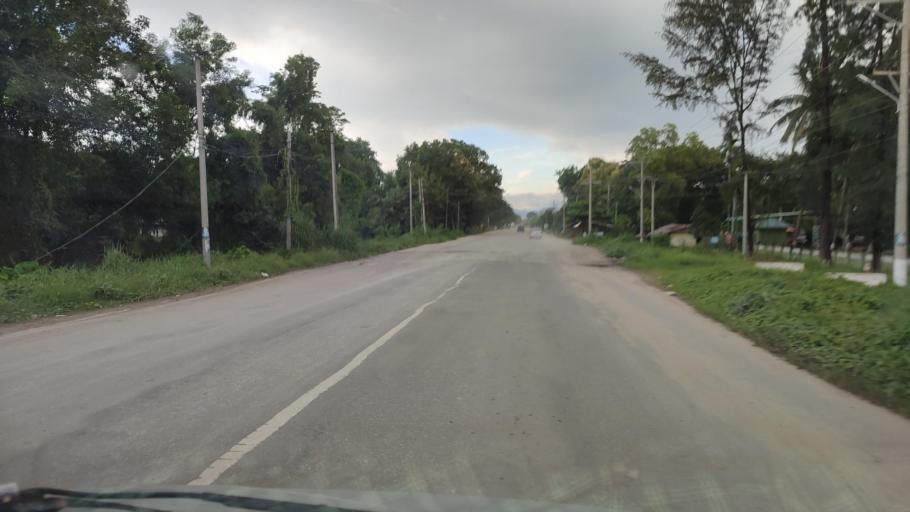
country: MM
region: Bago
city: Taungoo
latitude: 18.9026
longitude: 96.4323
